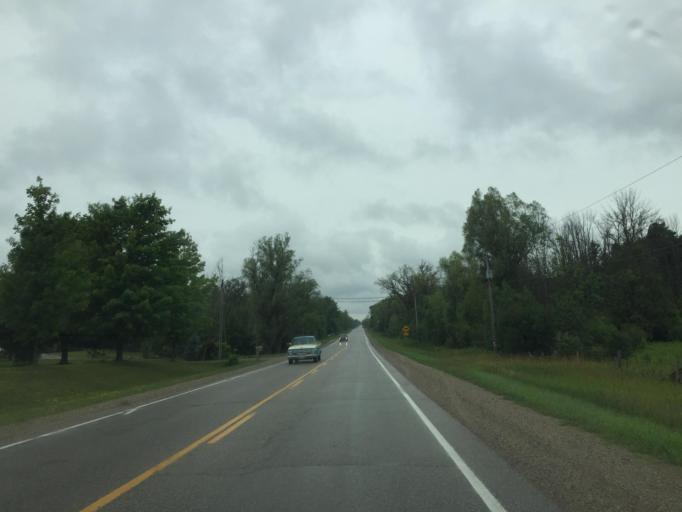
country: CA
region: Ontario
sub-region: Wellington County
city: Guelph
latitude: 43.4579
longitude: -80.2186
